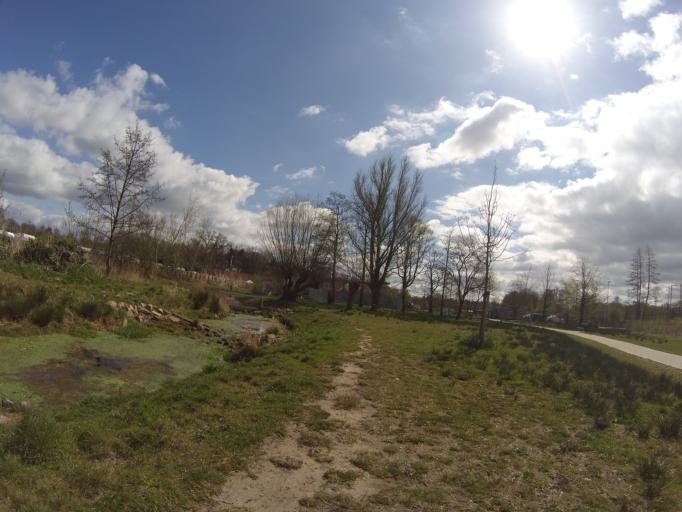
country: NL
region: Utrecht
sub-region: Gemeente Amersfoort
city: Randenbroek
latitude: 52.1419
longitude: 5.4034
